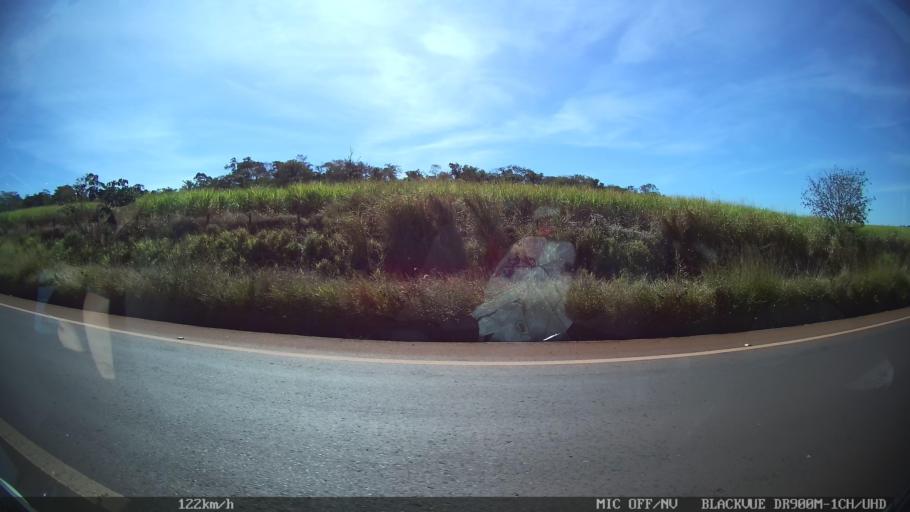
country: BR
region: Sao Paulo
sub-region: Sao Joaquim Da Barra
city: Sao Joaquim da Barra
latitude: -20.5404
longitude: -47.8109
